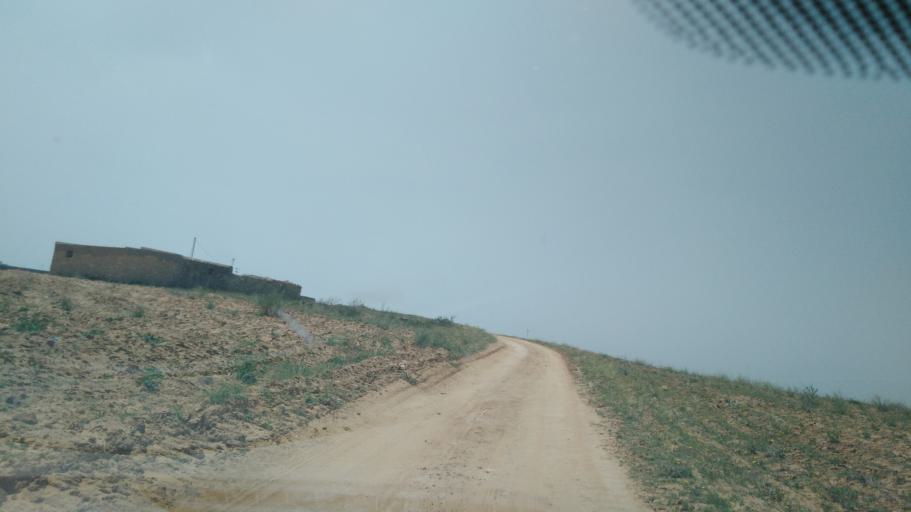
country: TN
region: Safaqis
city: Sfax
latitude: 34.7703
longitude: 10.5784
